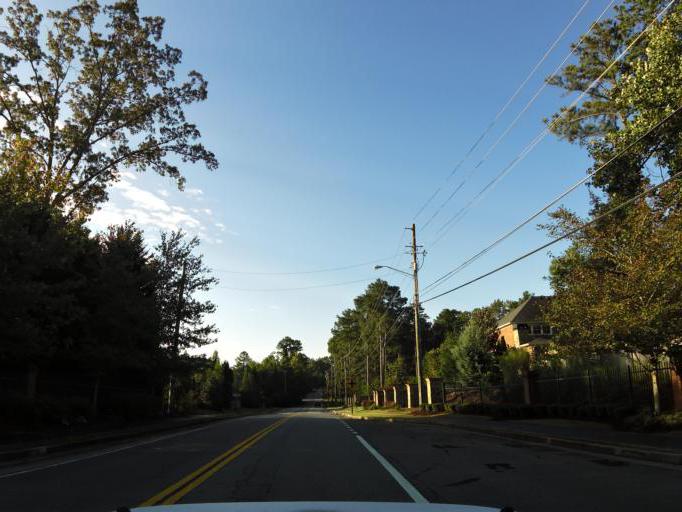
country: US
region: Georgia
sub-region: Cobb County
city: Kennesaw
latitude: 33.9686
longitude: -84.6173
